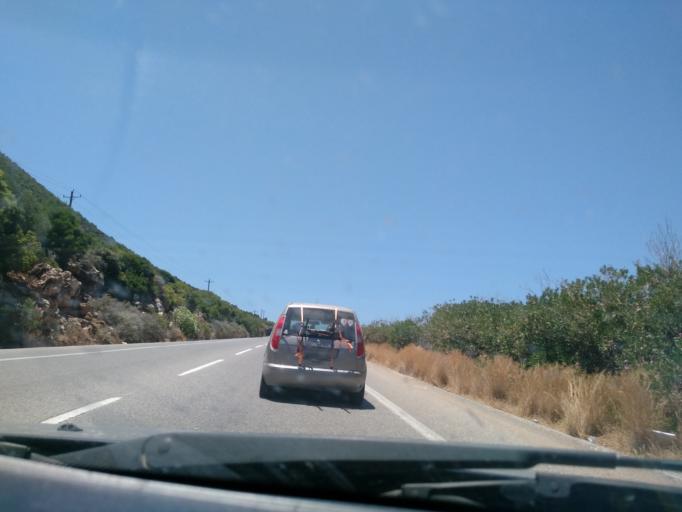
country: GR
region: Crete
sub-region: Nomos Rethymnis
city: Zoniana
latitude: 35.4060
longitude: 24.8324
